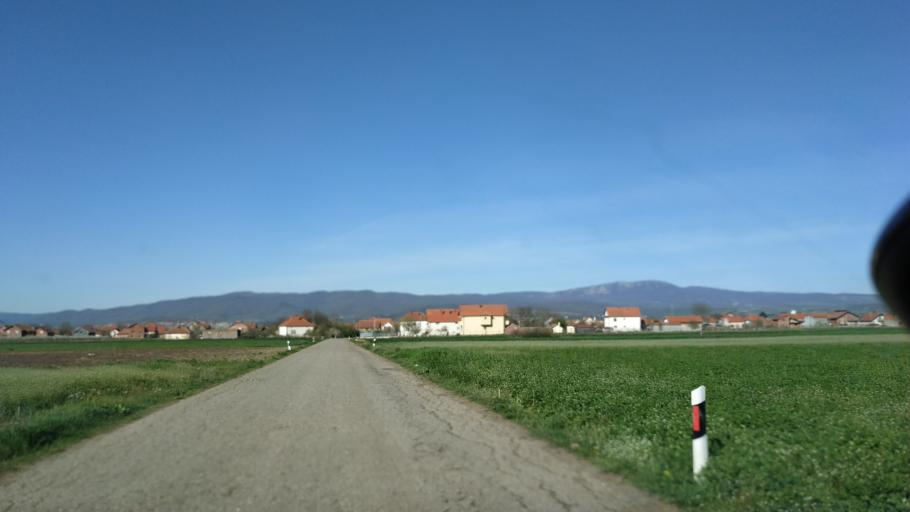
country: RS
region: Central Serbia
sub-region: Nisavski Okrug
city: Aleksinac
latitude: 43.5053
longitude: 21.6820
